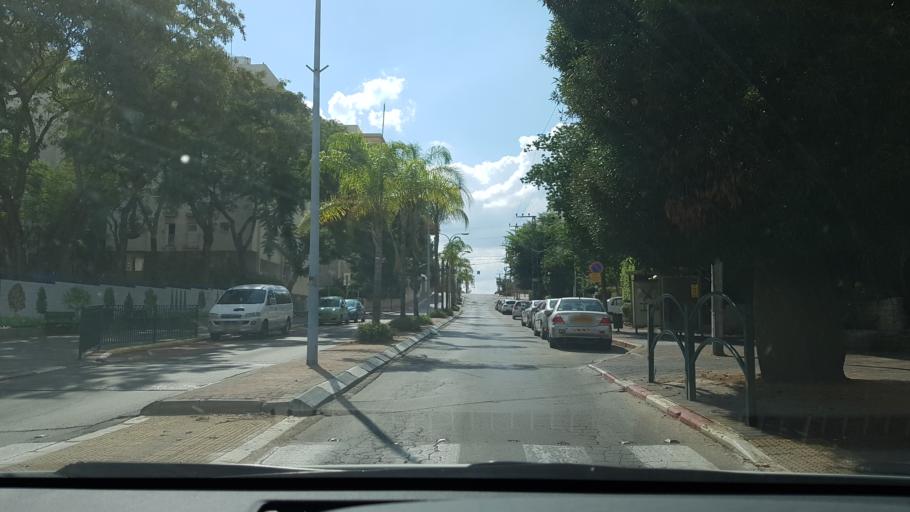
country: IL
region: Central District
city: Ness Ziona
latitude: 31.9037
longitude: 34.8146
